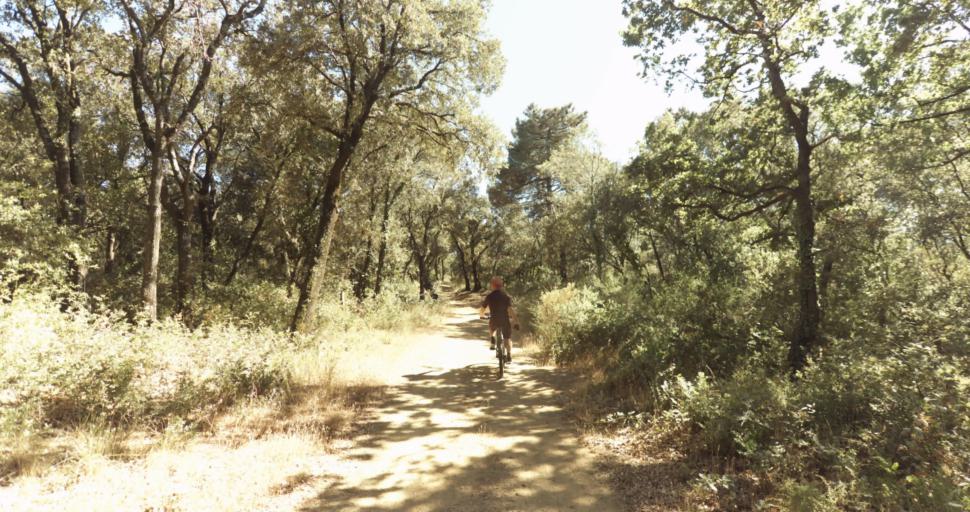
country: FR
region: Provence-Alpes-Cote d'Azur
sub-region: Departement du Var
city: Gassin
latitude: 43.2447
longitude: 6.5845
